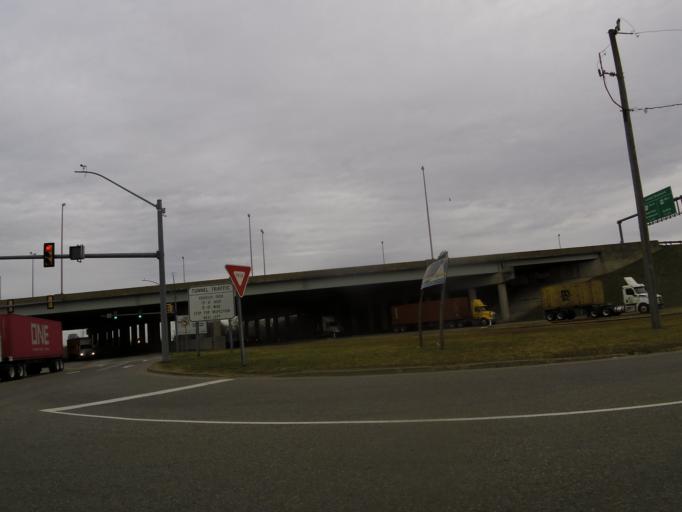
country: US
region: Virginia
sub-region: City of Portsmouth
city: Portsmouth
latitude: 36.8466
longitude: -76.3305
